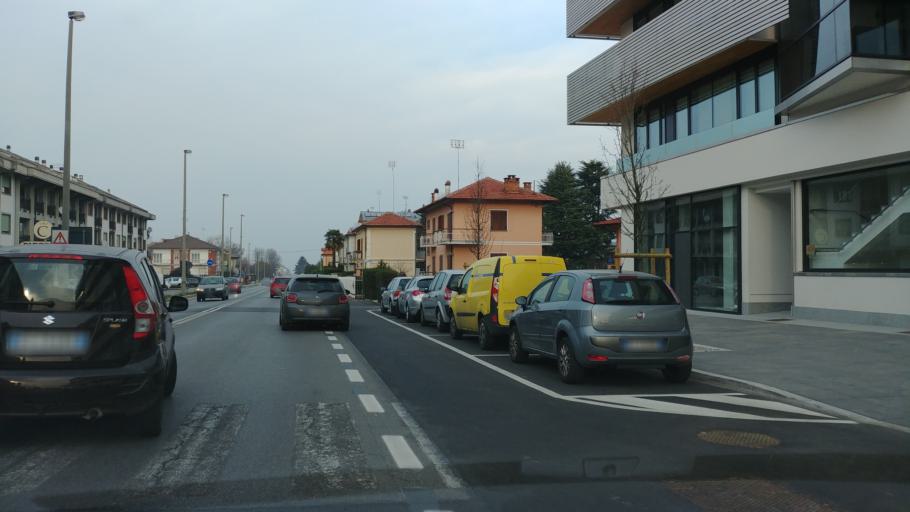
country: IT
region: Piedmont
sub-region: Provincia di Cuneo
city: Cuneo
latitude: 44.3659
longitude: 7.5237
